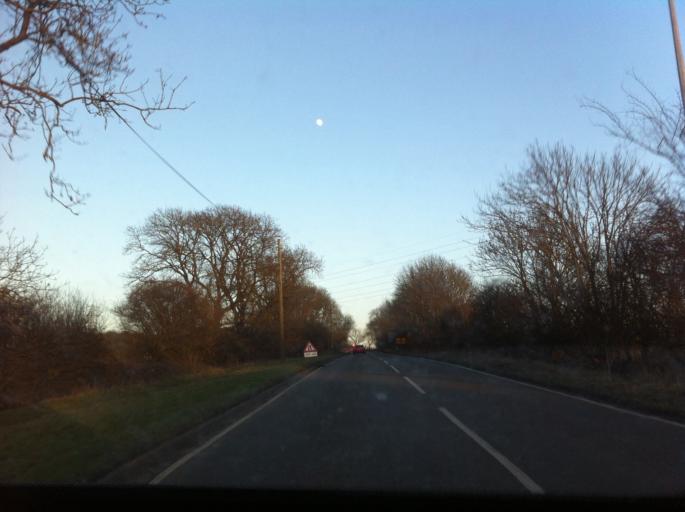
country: GB
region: England
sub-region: Northamptonshire
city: Wellingborough
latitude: 52.2826
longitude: -0.6768
